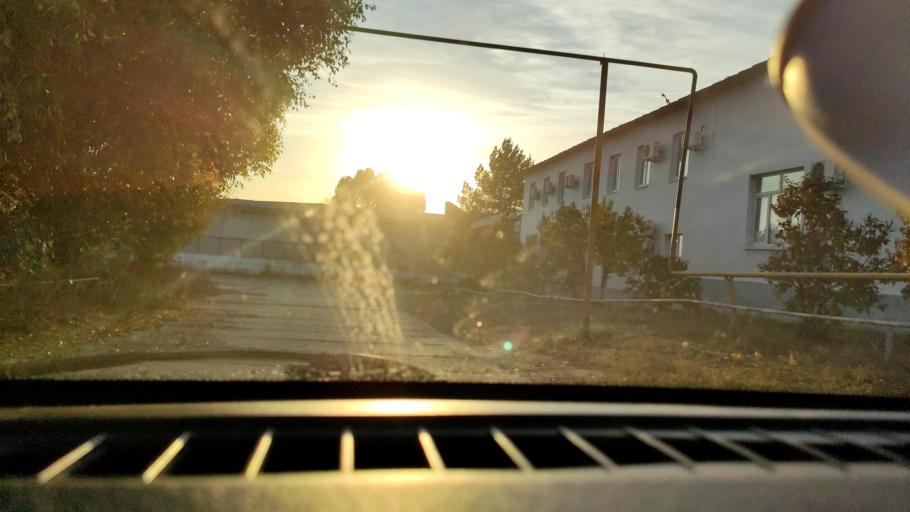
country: RU
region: Samara
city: Samara
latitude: 53.1782
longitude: 50.1616
